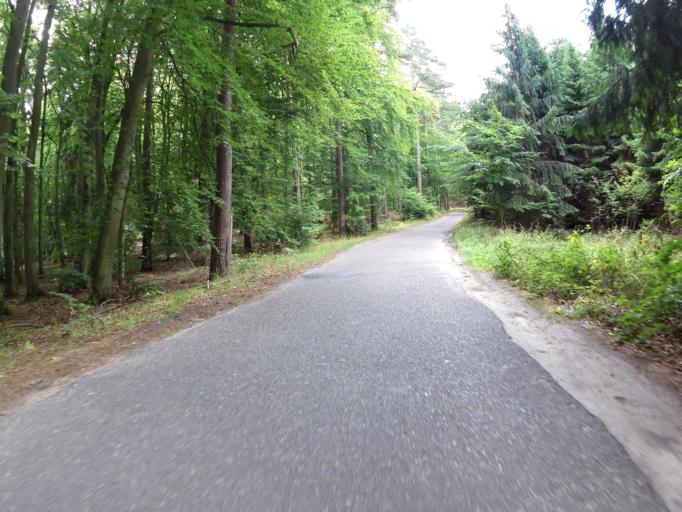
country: DE
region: Mecklenburg-Vorpommern
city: Seebad Bansin
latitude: 53.9815
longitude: 14.1089
